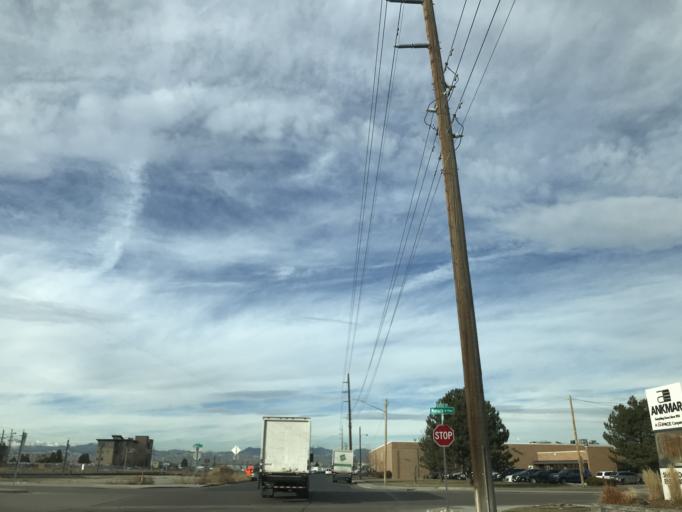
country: US
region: Colorado
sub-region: Adams County
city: Commerce City
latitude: 39.7740
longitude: -104.9124
